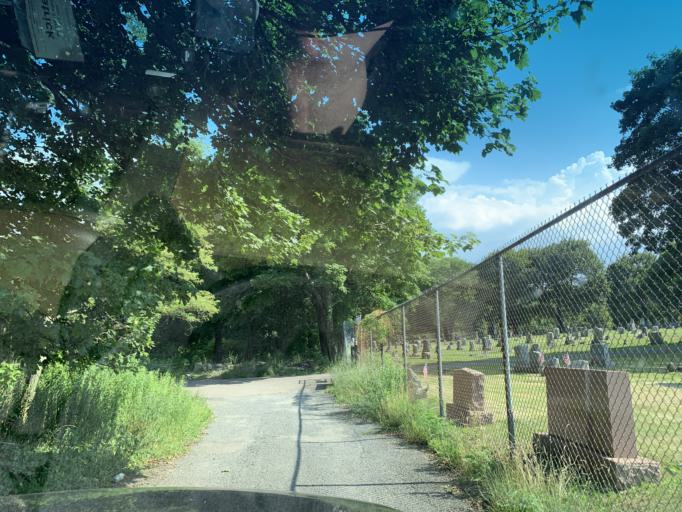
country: US
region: Pennsylvania
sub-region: Schuylkill County
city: Ashland
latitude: 40.8004
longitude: -76.3407
